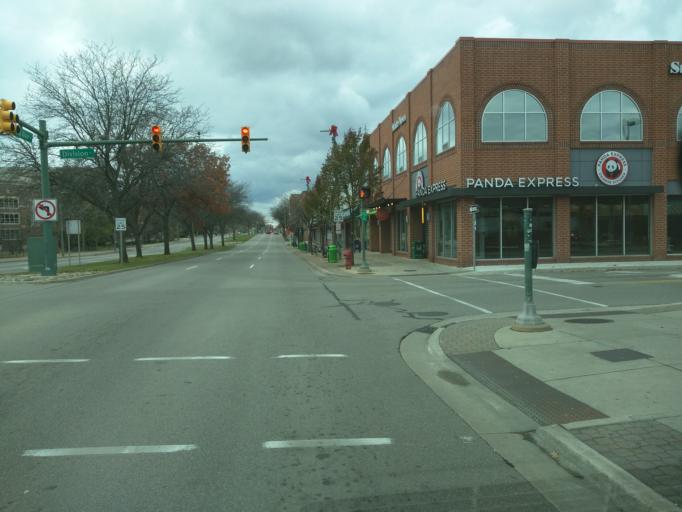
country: US
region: Michigan
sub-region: Ingham County
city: East Lansing
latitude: 42.7338
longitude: -84.4784
